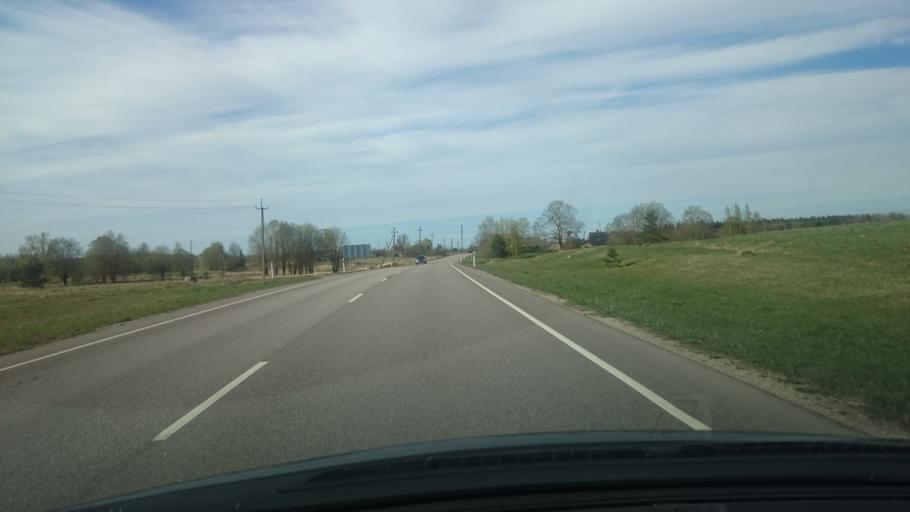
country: EE
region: Ida-Virumaa
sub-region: Johvi vald
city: Johvi
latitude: 59.2971
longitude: 27.4950
